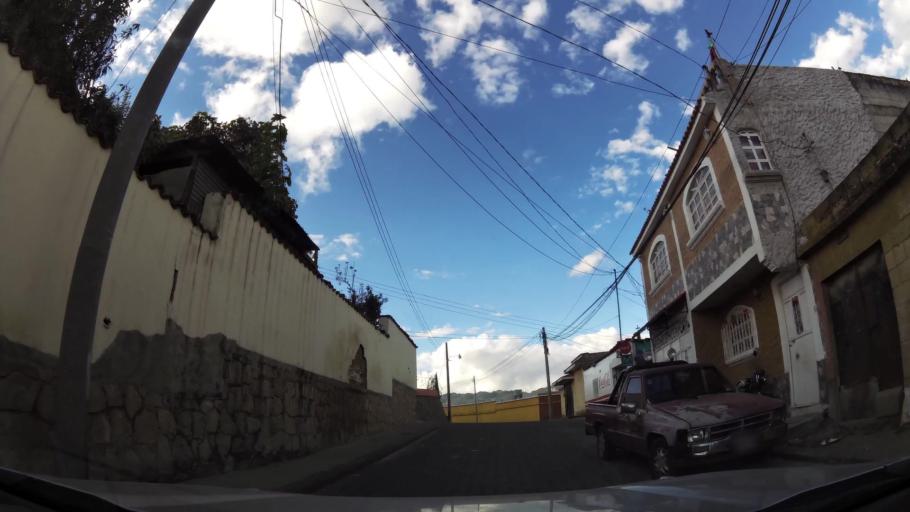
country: GT
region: Quetzaltenango
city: Quetzaltenango
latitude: 14.8514
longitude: -91.5242
